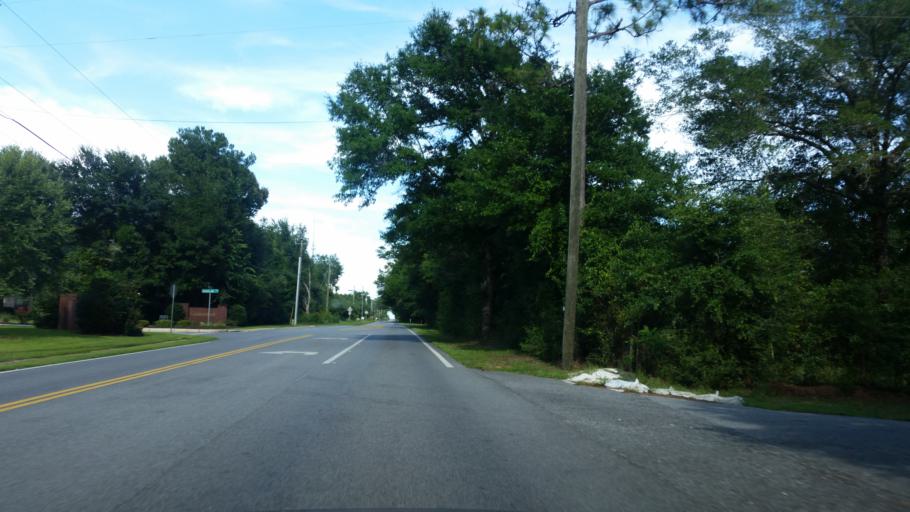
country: US
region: Florida
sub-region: Santa Rosa County
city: Milton
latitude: 30.6210
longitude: -87.0961
